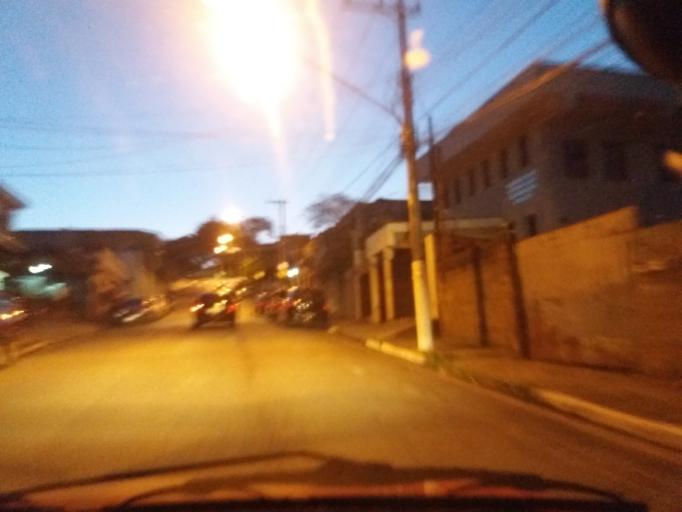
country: BR
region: Sao Paulo
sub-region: Taboao Da Serra
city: Taboao da Serra
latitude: -23.6182
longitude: -46.7447
